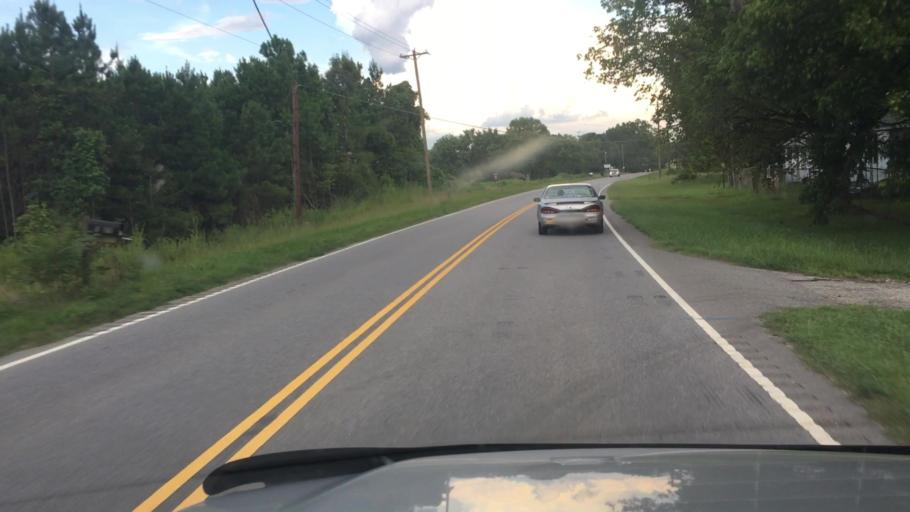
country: US
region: South Carolina
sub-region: Cherokee County
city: Gaffney
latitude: 35.1256
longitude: -81.7299
